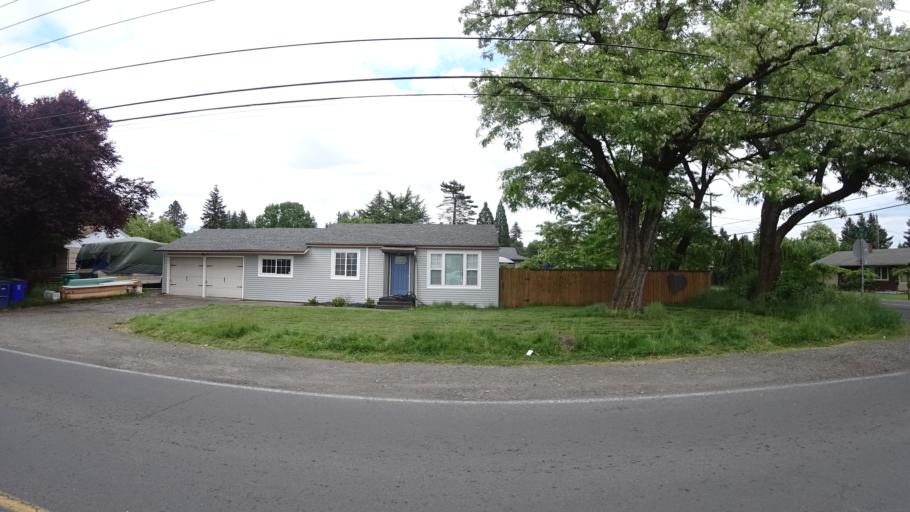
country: US
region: Oregon
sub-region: Multnomah County
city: Gresham
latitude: 45.5139
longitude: -122.4848
